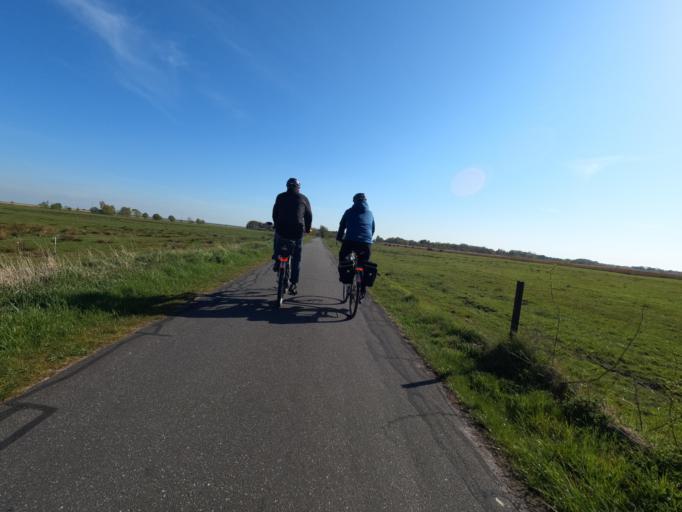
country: DE
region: Mecklenburg-Vorpommern
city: Ostseebad Prerow
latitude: 54.4211
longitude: 12.6134
